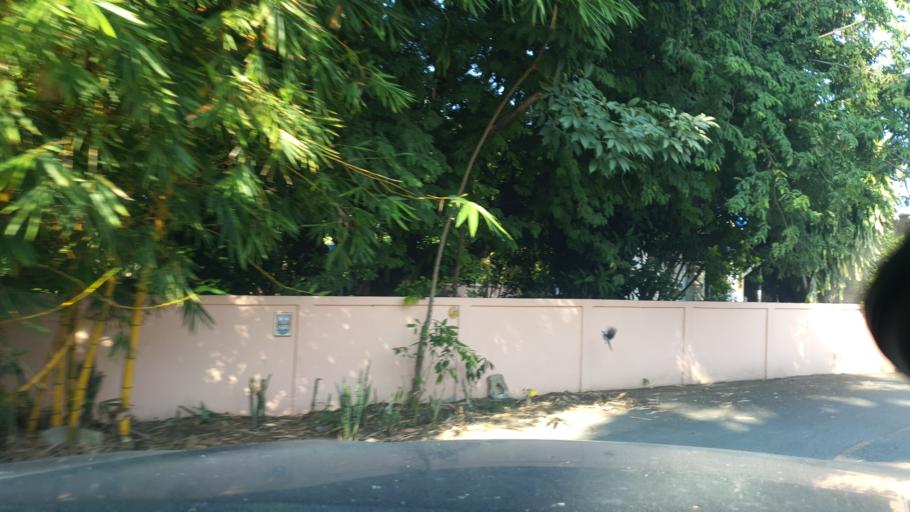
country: TH
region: Chiang Mai
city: San Kamphaeng
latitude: 18.7513
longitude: 99.1469
